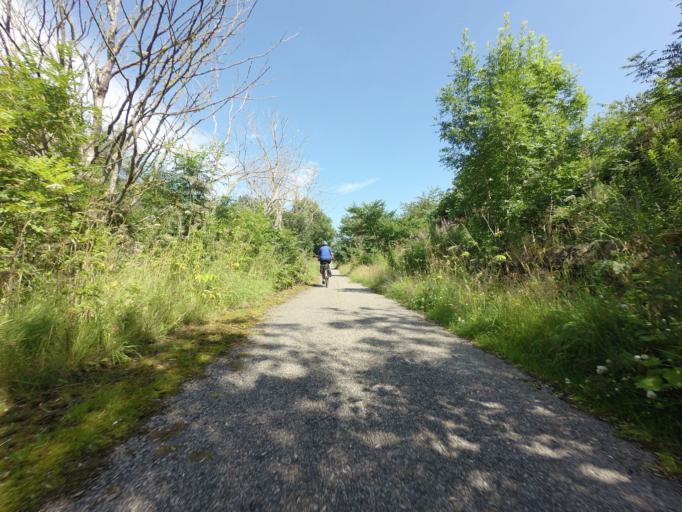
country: GB
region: Scotland
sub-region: Highland
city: Dingwall
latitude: 57.5857
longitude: -4.4297
